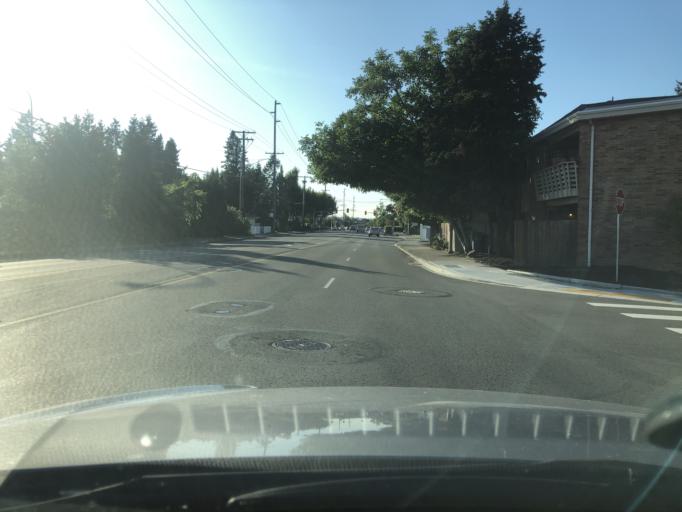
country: US
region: Washington
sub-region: King County
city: Auburn
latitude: 47.3185
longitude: -122.2180
